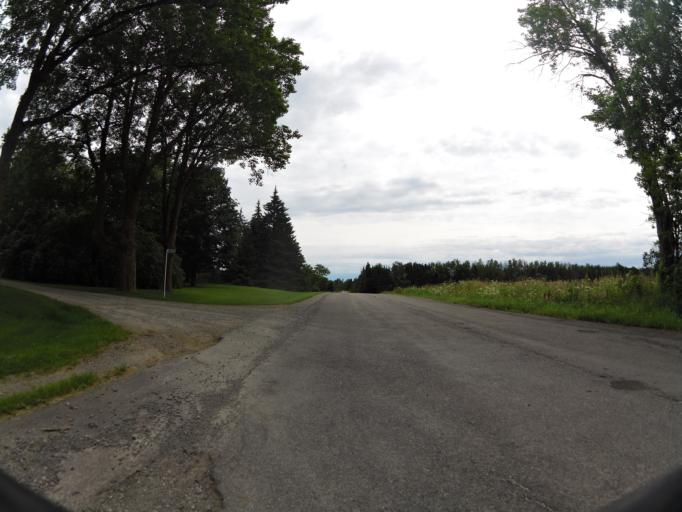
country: CA
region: Ontario
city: Bells Corners
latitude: 45.1023
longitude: -75.5923
